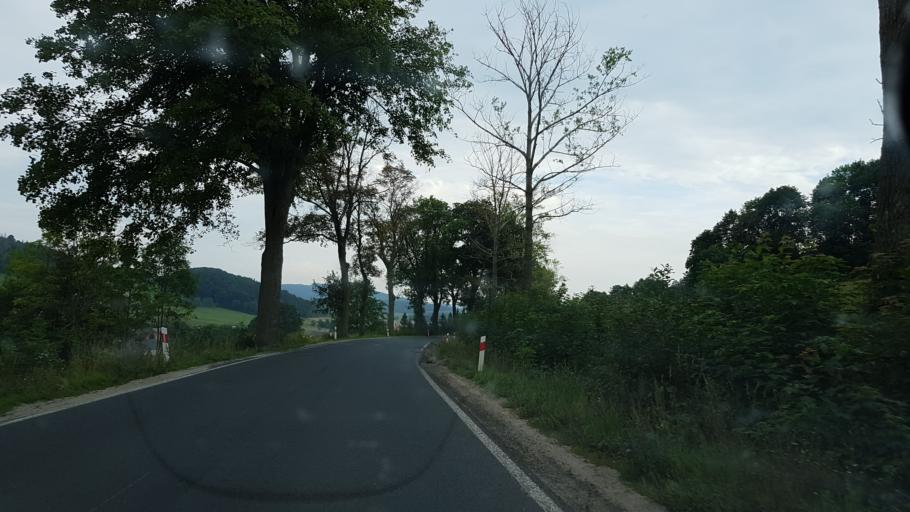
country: PL
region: Lower Silesian Voivodeship
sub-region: Powiat kamiennogorski
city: Marciszow
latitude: 50.8918
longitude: 15.9924
